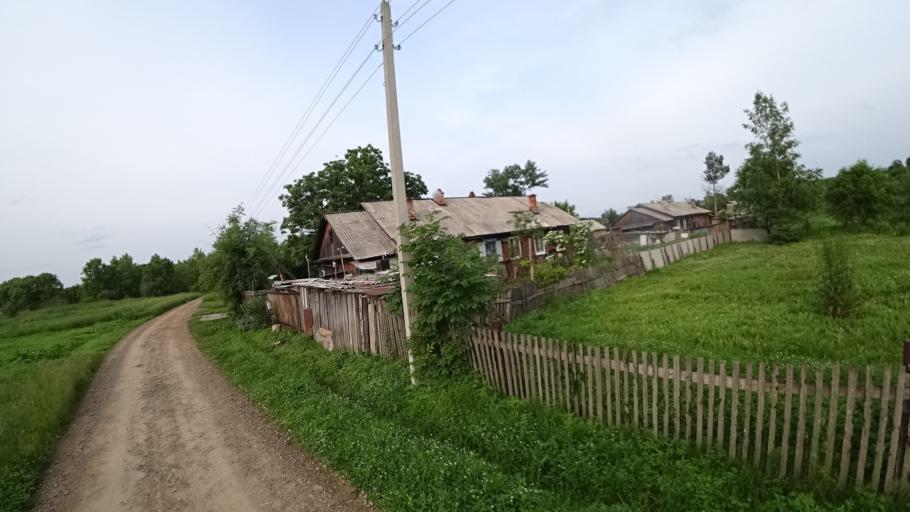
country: RU
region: Primorskiy
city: Novosysoyevka
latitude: 44.2446
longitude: 133.3608
